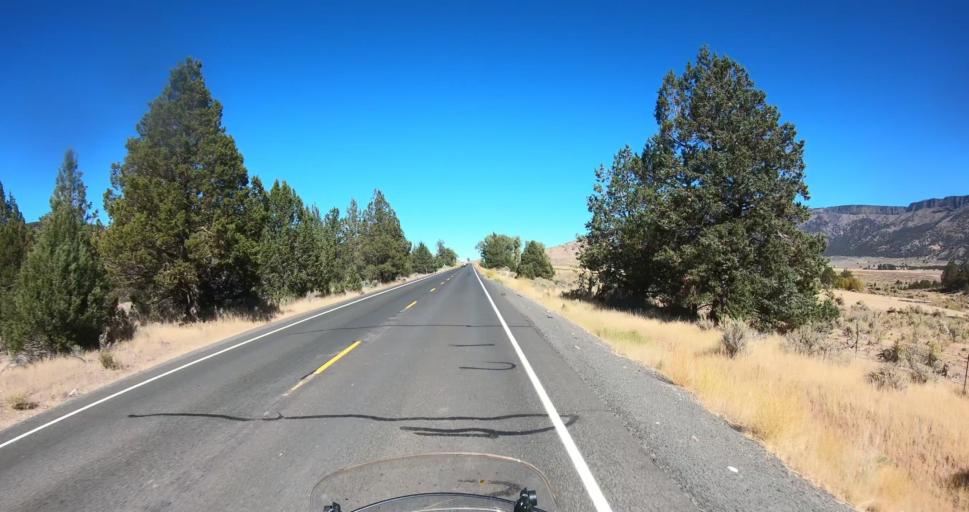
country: US
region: Oregon
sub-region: Lake County
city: Lakeview
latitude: 42.4332
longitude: -120.2816
